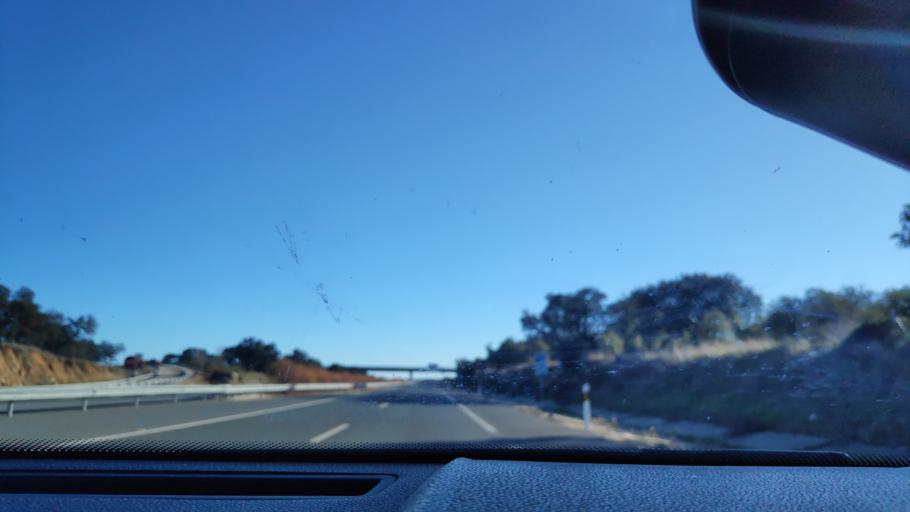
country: ES
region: Andalusia
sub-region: Provincia de Huelva
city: Santa Olalla del Cala
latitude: 37.9537
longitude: -6.2314
